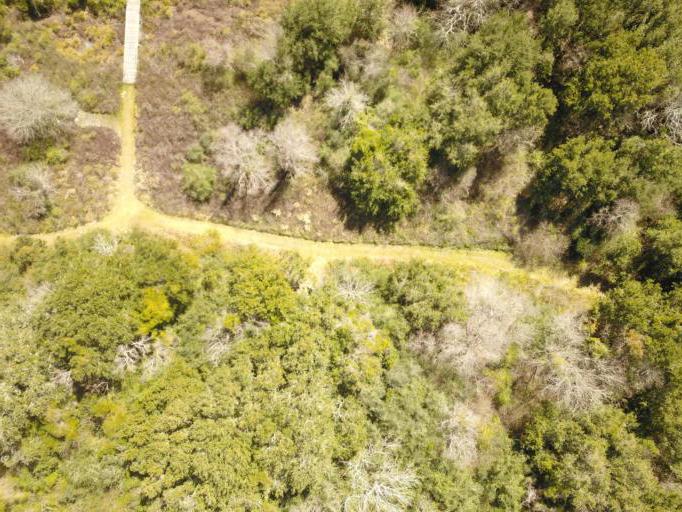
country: US
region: Texas
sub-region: Galveston County
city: Bolivar Peninsula
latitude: 29.5603
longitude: -94.3895
